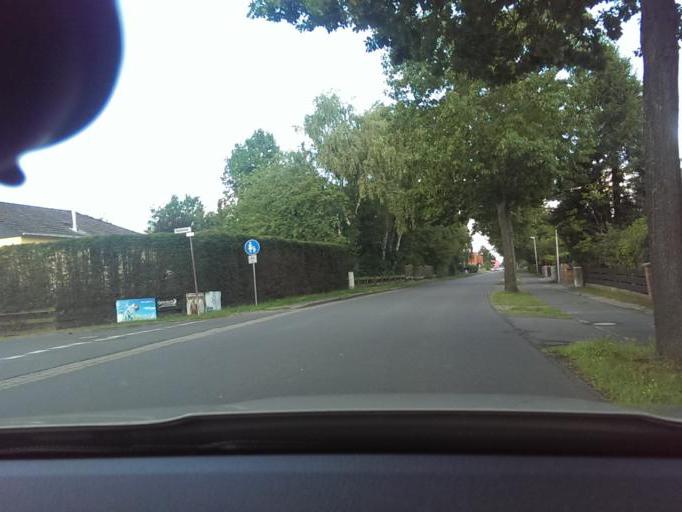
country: DE
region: Lower Saxony
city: Isernhagen Farster Bauerschaft
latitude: 52.4596
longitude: 9.8260
